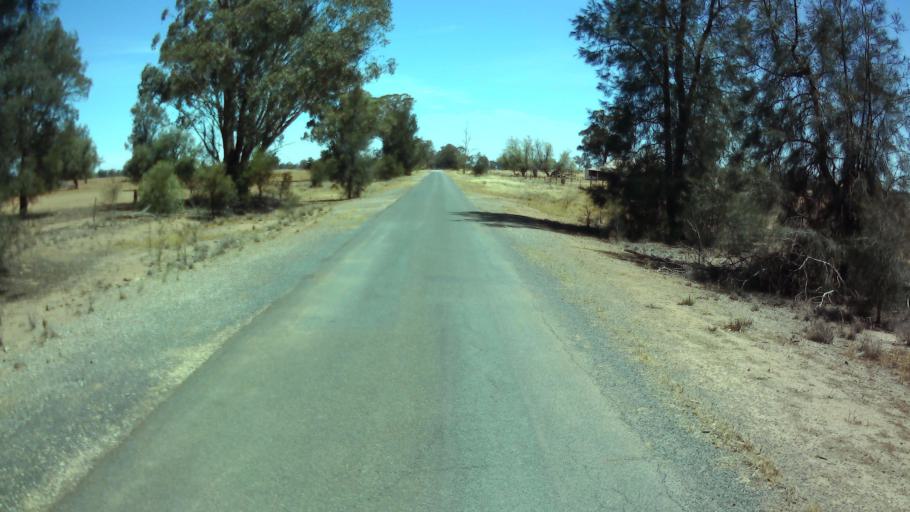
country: AU
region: New South Wales
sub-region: Weddin
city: Grenfell
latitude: -33.9042
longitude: 147.6858
